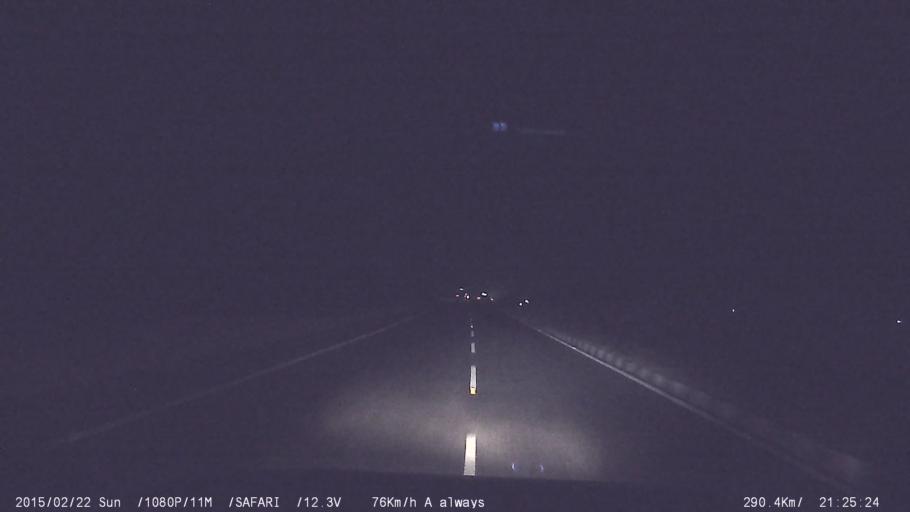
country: IN
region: Tamil Nadu
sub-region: Karur
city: Karur
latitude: 10.8956
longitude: 78.0280
